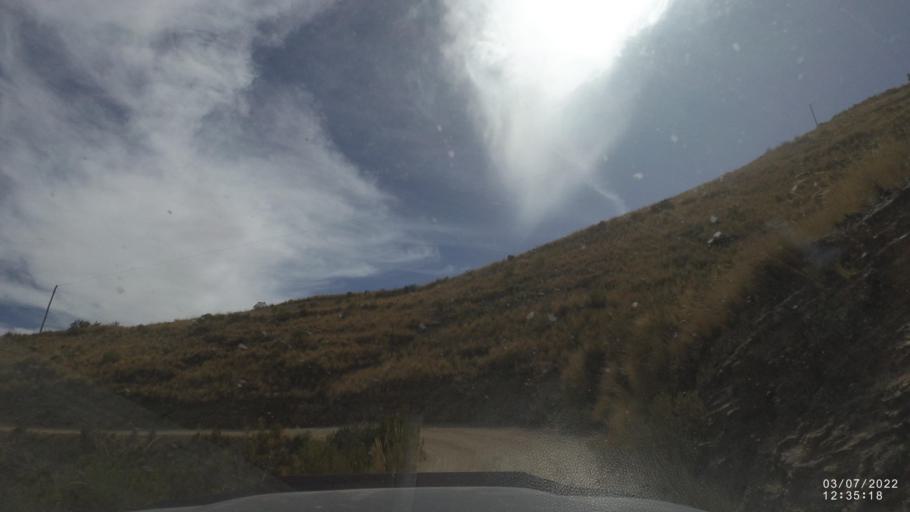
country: BO
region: Cochabamba
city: Irpa Irpa
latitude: -17.8054
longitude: -66.6079
